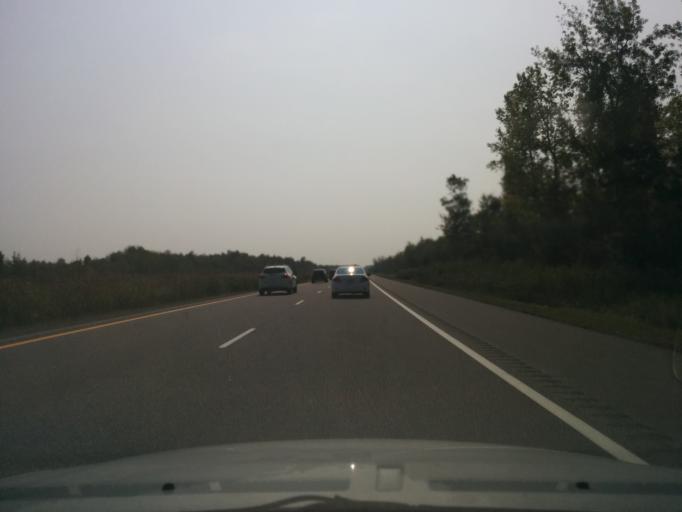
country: CA
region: Ontario
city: Bells Corners
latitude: 45.0786
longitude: -75.6300
